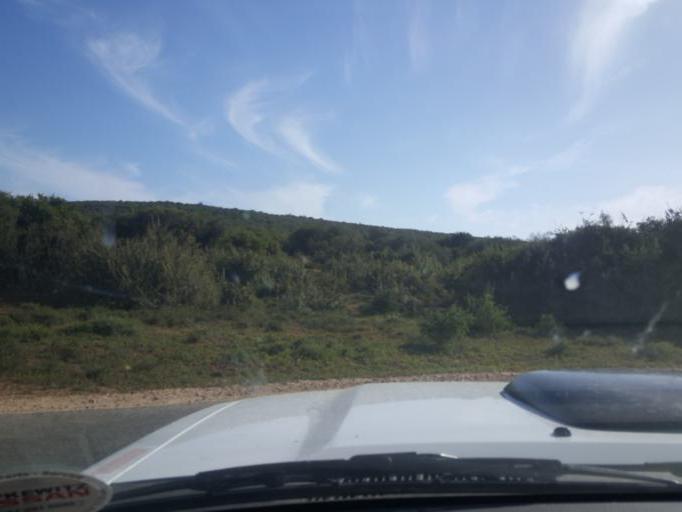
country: ZA
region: Eastern Cape
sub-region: Cacadu District Municipality
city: Kirkwood
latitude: -33.4417
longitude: 25.7642
